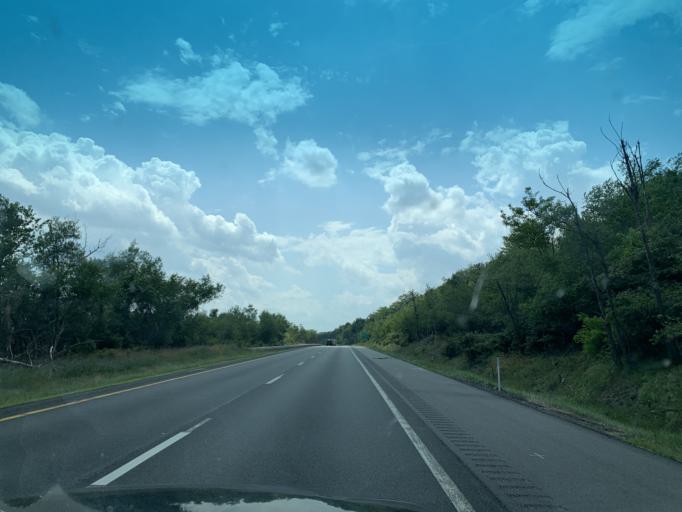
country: US
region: Pennsylvania
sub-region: Schuylkill County
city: Hometown
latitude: 40.8518
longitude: -76.0500
